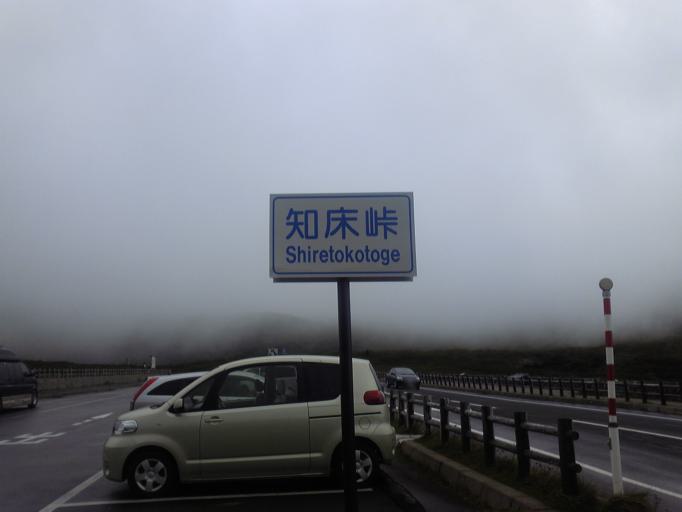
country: JP
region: Hokkaido
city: Shibetsu
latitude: 44.0530
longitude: 145.1043
